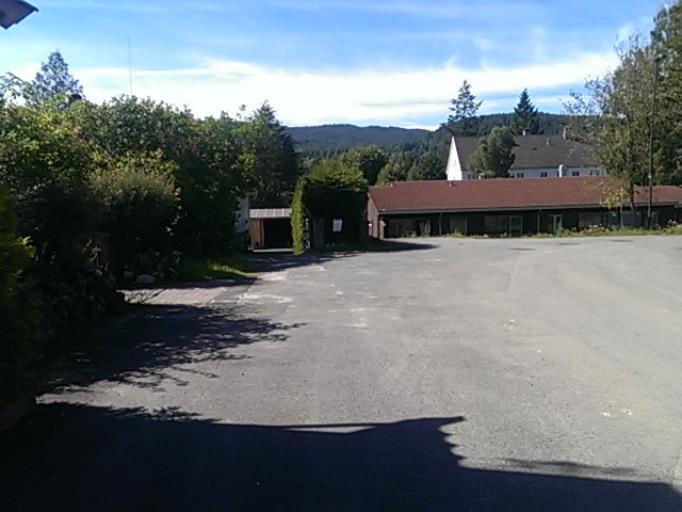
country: NO
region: Buskerud
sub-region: Kongsberg
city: Kongsberg
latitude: 59.6603
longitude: 9.6568
